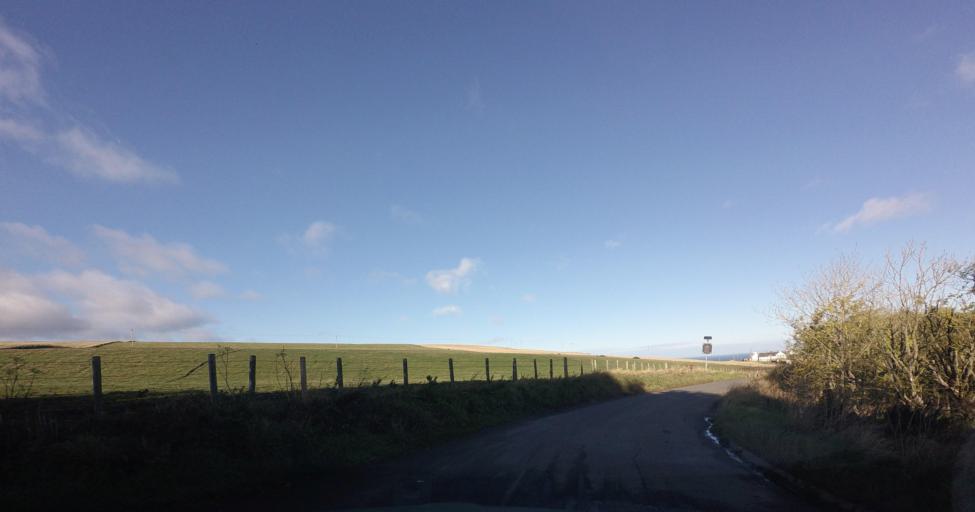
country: GB
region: Scotland
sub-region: Aberdeenshire
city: Macduff
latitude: 57.6637
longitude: -2.3229
